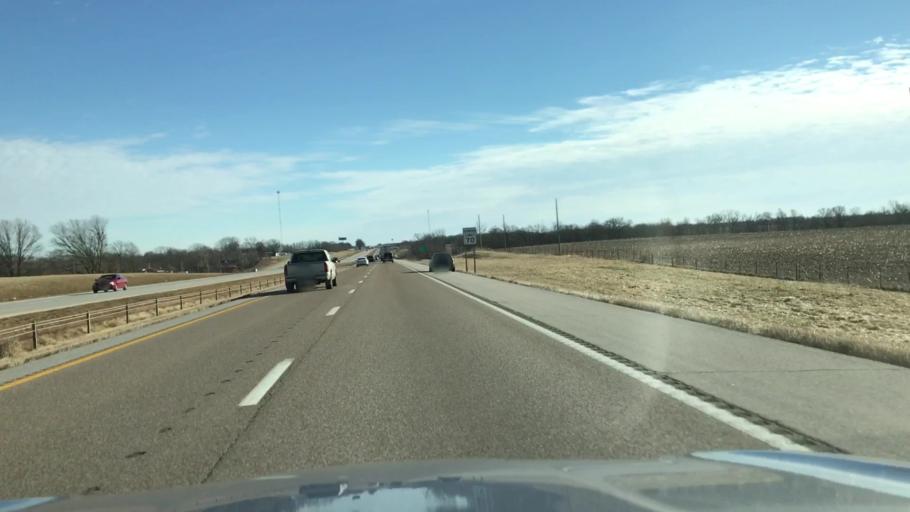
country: US
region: Missouri
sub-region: Cooper County
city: Boonville
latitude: 38.9349
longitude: -92.8364
